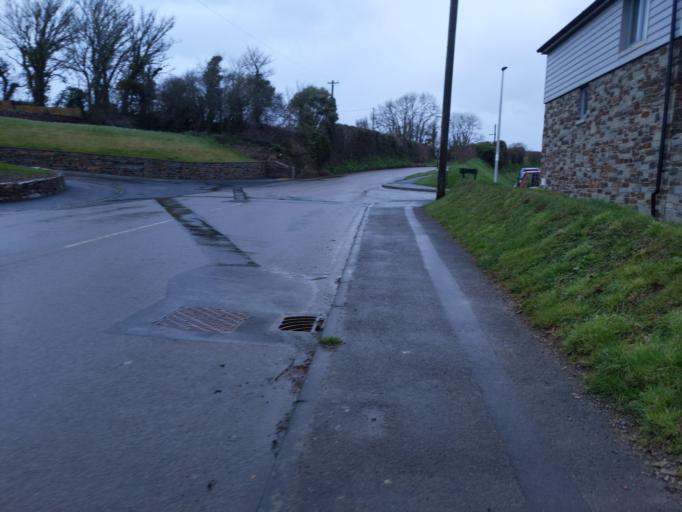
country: GB
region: England
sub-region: Devon
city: Wembury
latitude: 50.3198
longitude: -4.0348
